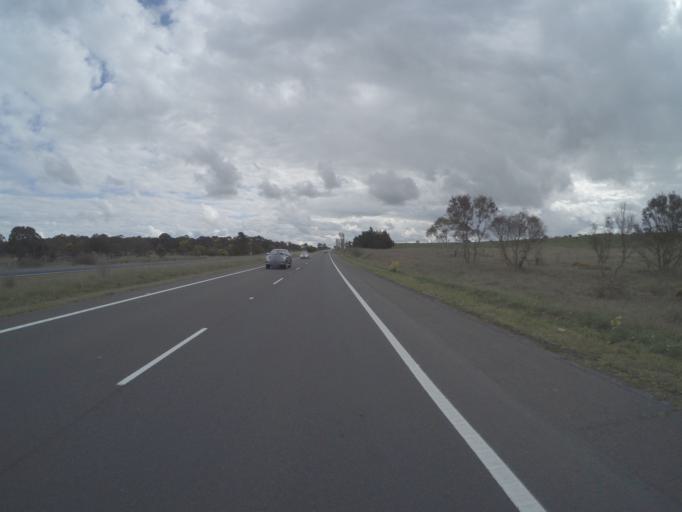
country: AU
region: New South Wales
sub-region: Goulburn Mulwaree
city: Goulburn
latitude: -34.8075
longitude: 149.5999
